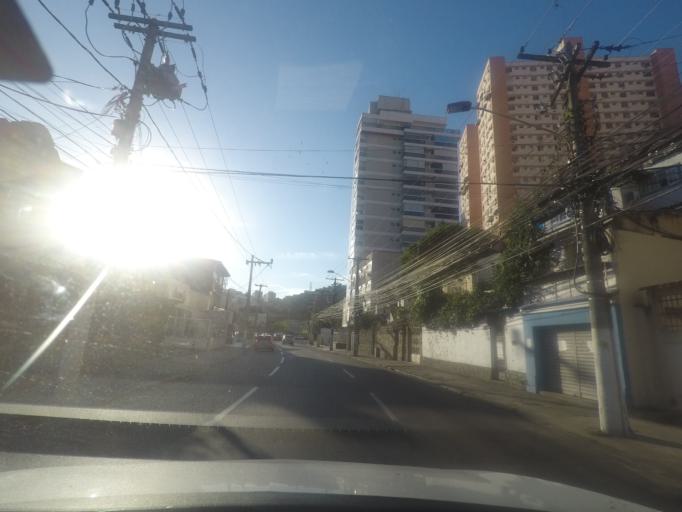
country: BR
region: Rio de Janeiro
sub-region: Niteroi
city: Niteroi
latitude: -22.8994
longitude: -43.1097
